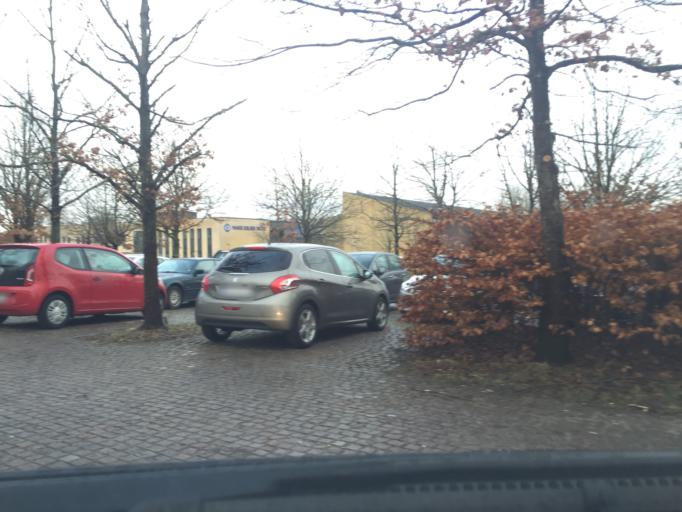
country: DK
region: Capital Region
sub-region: Fureso Kommune
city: Stavnsholt
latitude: 55.8137
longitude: 12.3856
